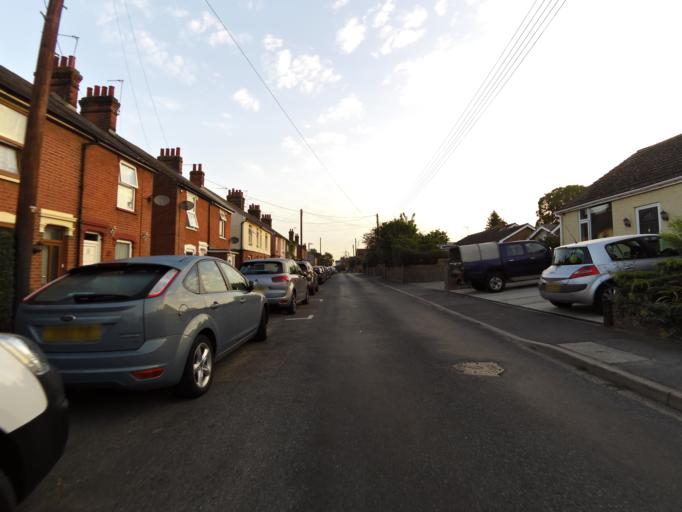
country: GB
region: England
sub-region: Suffolk
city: Bramford
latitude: 52.0772
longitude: 1.1066
